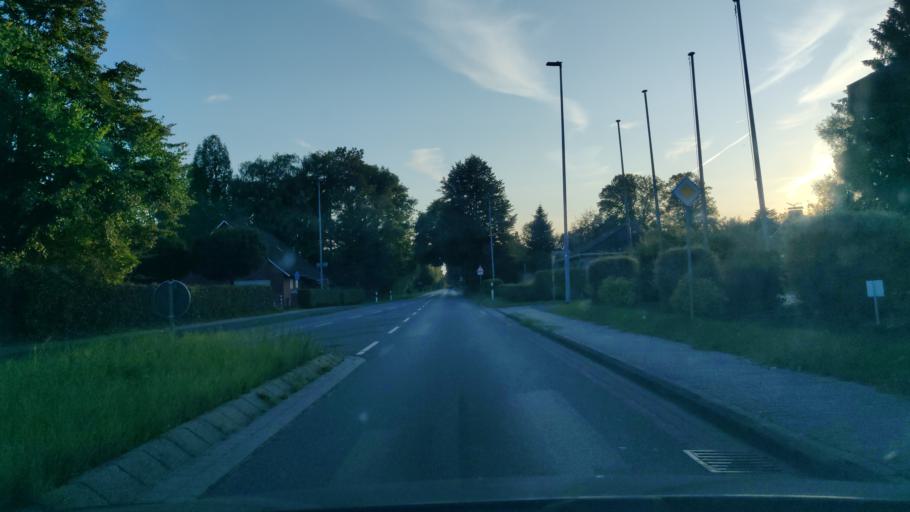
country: DE
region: Lower Saxony
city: Aurich
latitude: 53.4599
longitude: 7.4543
